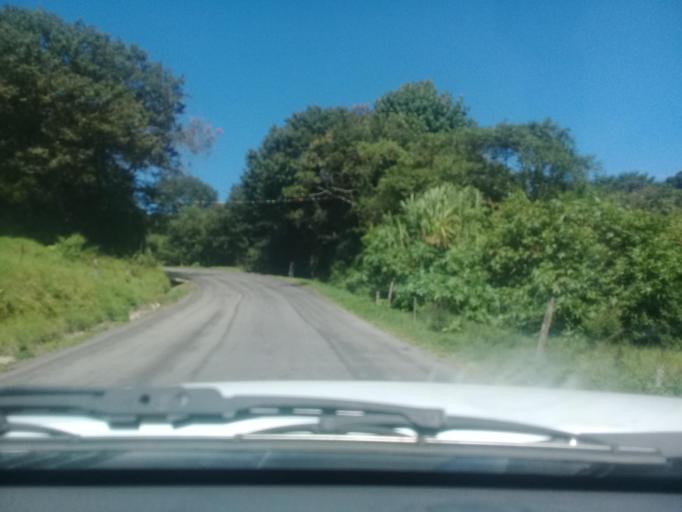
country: MX
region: Veracruz
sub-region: Tlalnelhuayocan
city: Otilpan
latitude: 19.5671
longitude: -96.9857
